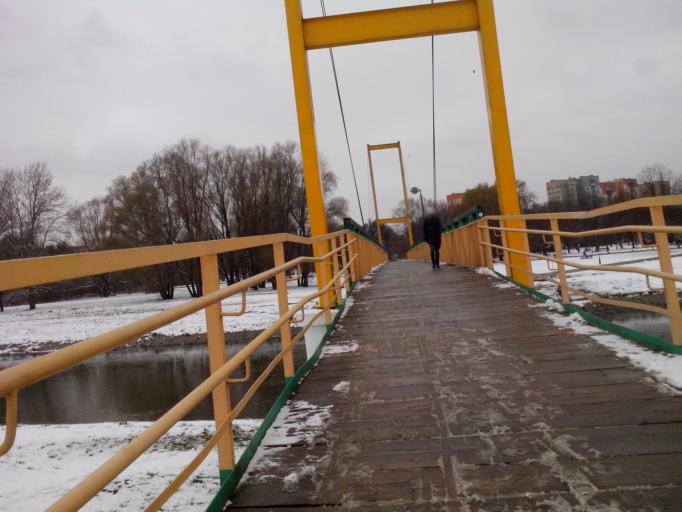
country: PL
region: Subcarpathian Voivodeship
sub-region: Rzeszow
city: Rzeszow
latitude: 50.0241
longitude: 22.0026
